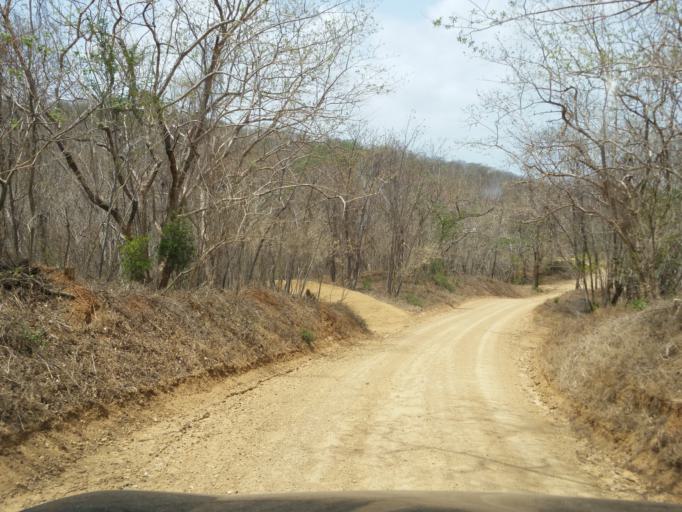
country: NI
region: Rivas
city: Tola
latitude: 11.4253
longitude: -86.0626
